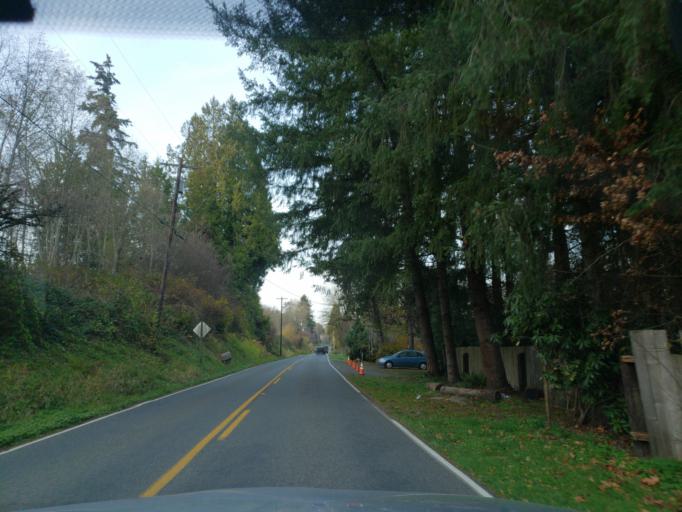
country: US
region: Washington
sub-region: Snohomish County
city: Cathcart
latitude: 47.8463
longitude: -122.0927
